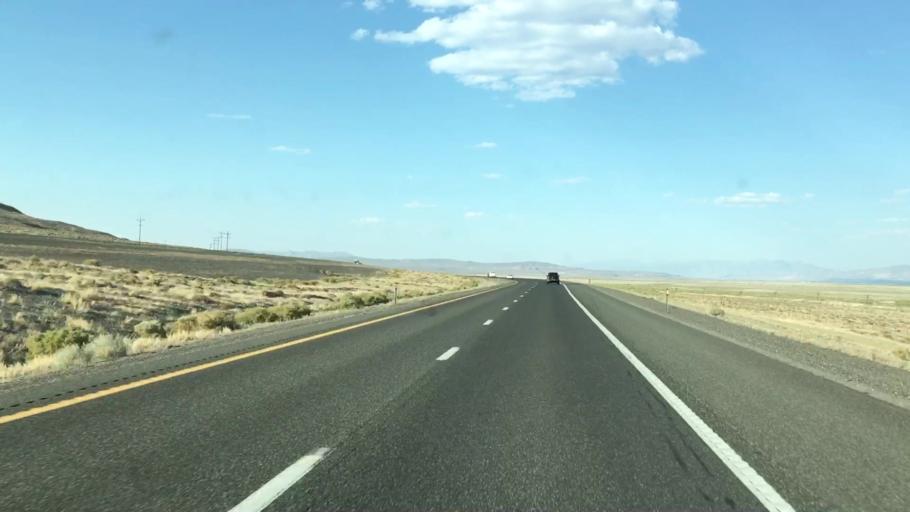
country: US
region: Nevada
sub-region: Pershing County
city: Lovelock
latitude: 39.9861
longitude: -118.6859
